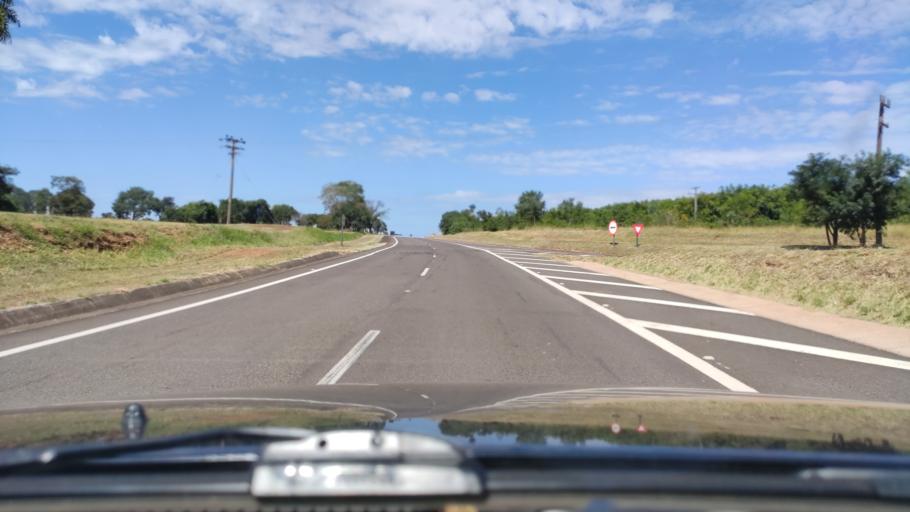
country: BR
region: Sao Paulo
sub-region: Rancharia
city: Rancharia
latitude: -22.4427
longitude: -50.9966
